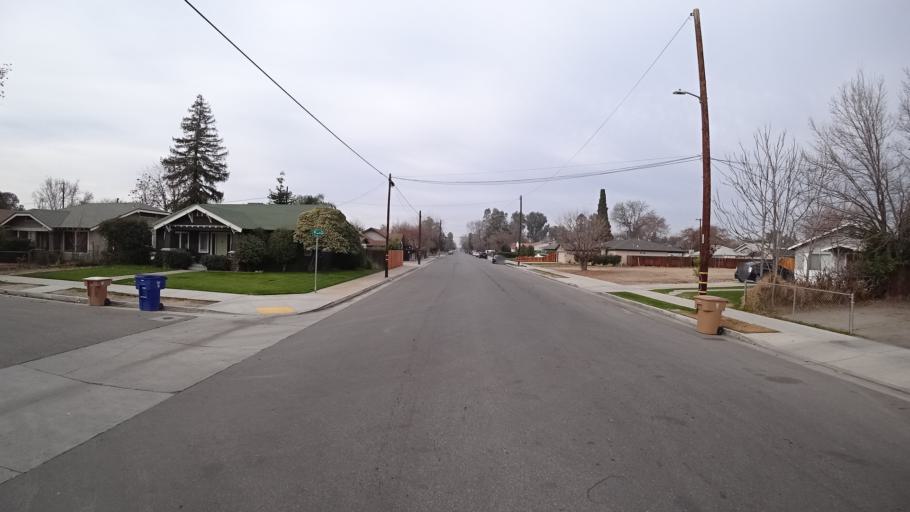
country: US
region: California
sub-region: Kern County
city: Bakersfield
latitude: 35.3631
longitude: -119.0222
